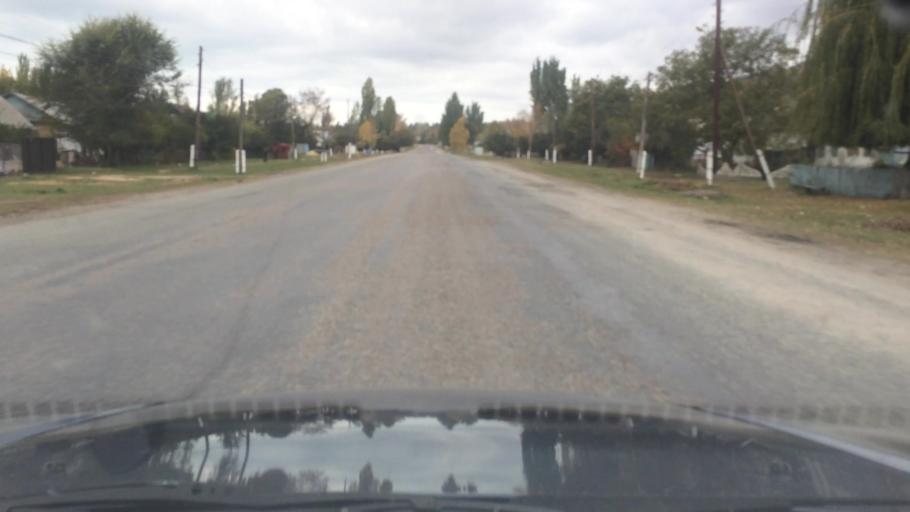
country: KG
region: Ysyk-Koel
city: Tyup
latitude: 42.7550
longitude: 78.1376
